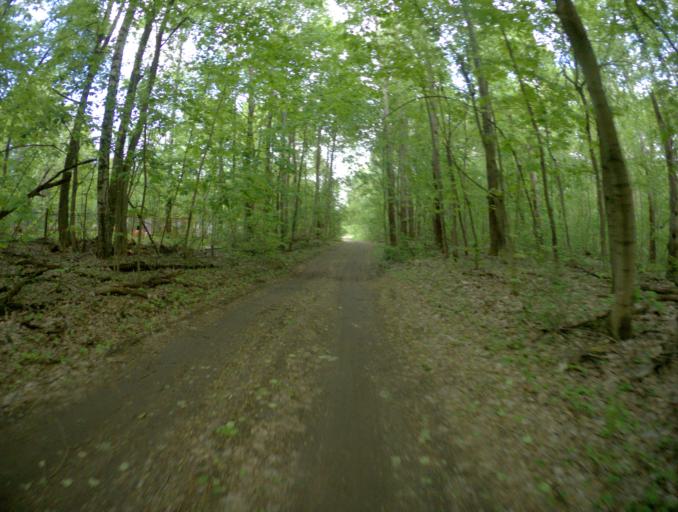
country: RU
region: Rjazan
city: Spas-Klepiki
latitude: 55.2533
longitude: 40.1103
